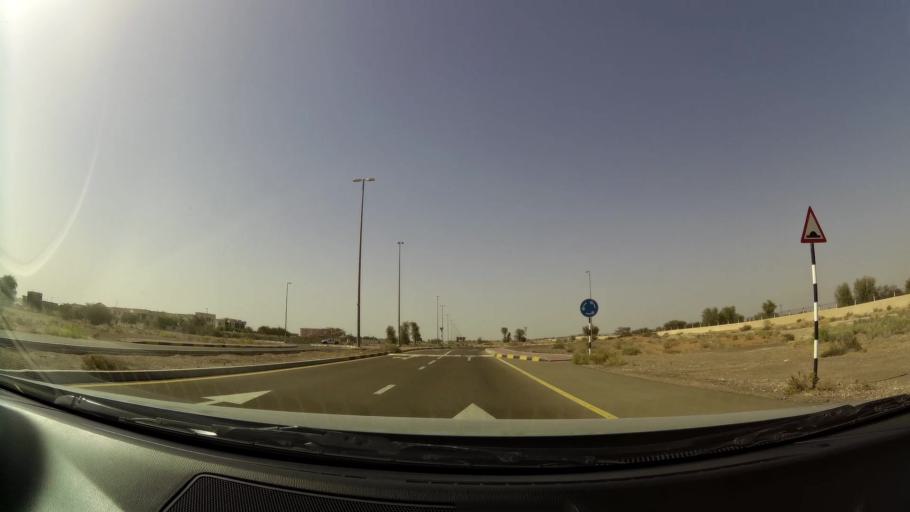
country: OM
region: Al Buraimi
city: Al Buraymi
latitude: 24.3298
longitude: 55.7833
